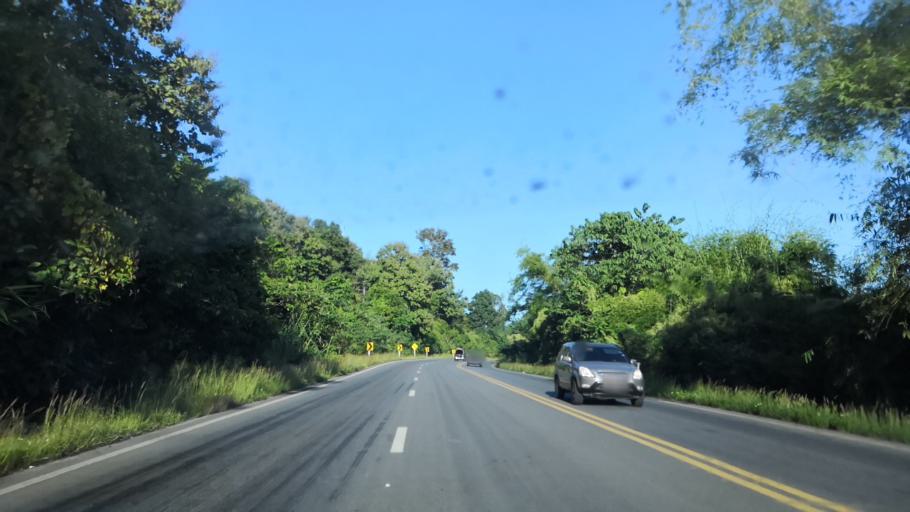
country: TH
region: Chiang Rai
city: Mae Suai
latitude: 19.7246
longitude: 99.6100
